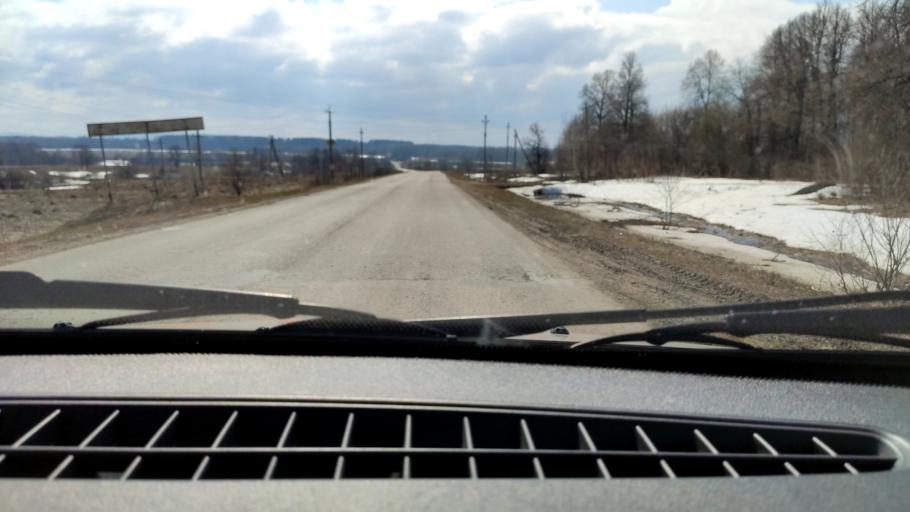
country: RU
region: Bashkortostan
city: Kudeyevskiy
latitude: 54.8267
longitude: 56.7929
